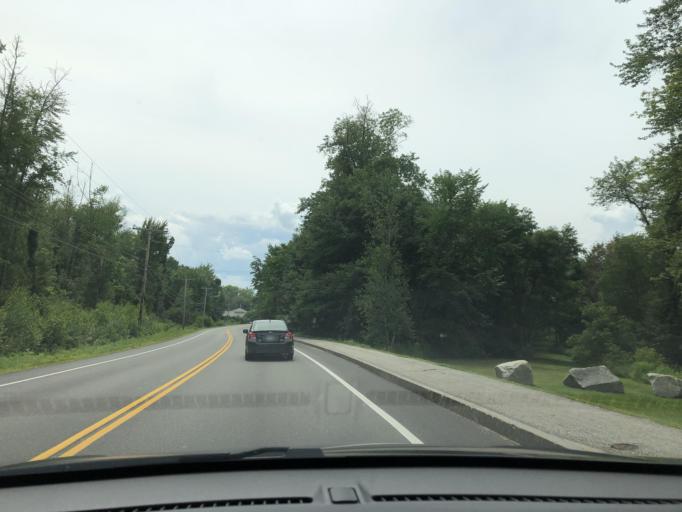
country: US
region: New Hampshire
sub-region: Merrimack County
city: Concord
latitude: 43.1962
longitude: -71.5191
